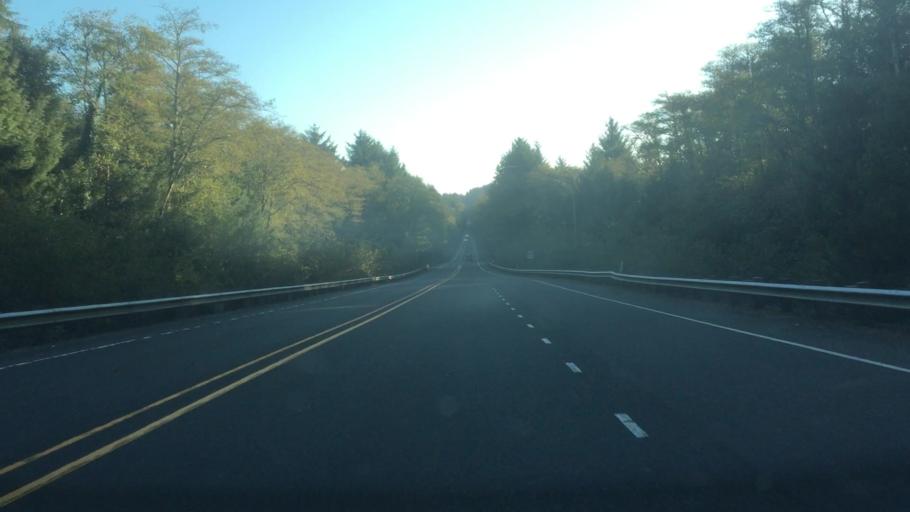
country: US
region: Oregon
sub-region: Clatsop County
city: Cannon Beach
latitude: 45.9009
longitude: -123.9534
